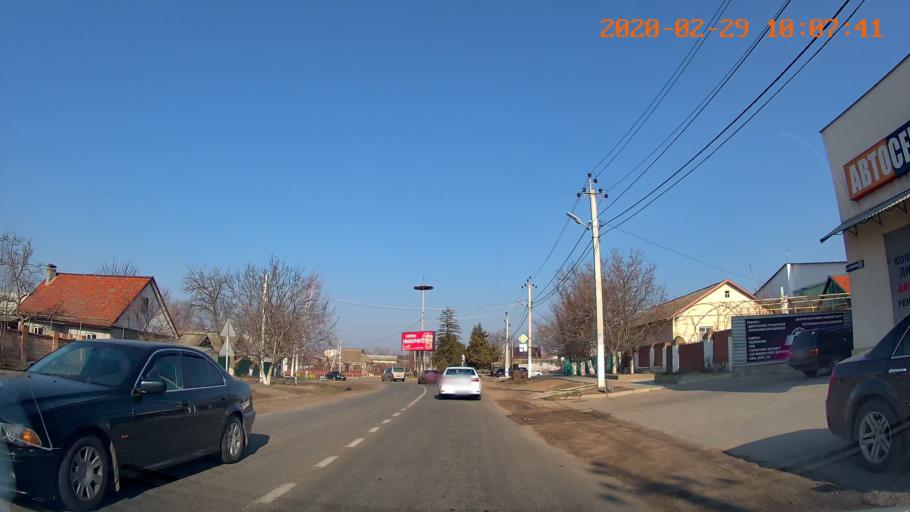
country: MD
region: Telenesti
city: Tiraspolul Nou
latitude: 46.8225
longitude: 29.6640
